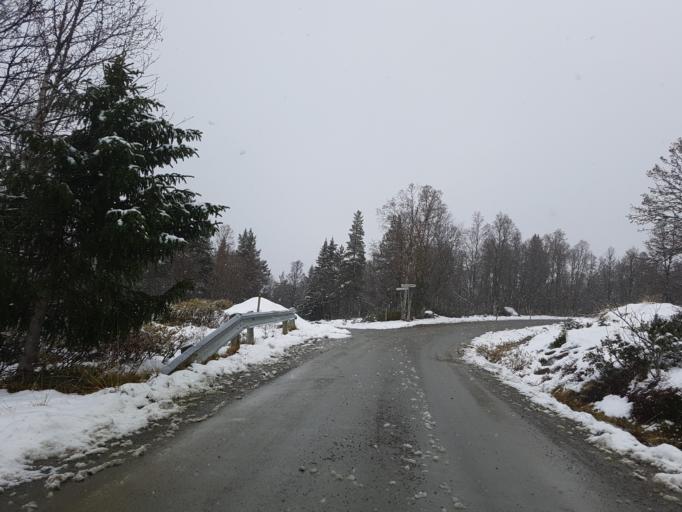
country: NO
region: Oppland
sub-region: Sel
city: Otta
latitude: 61.7902
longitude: 9.7192
